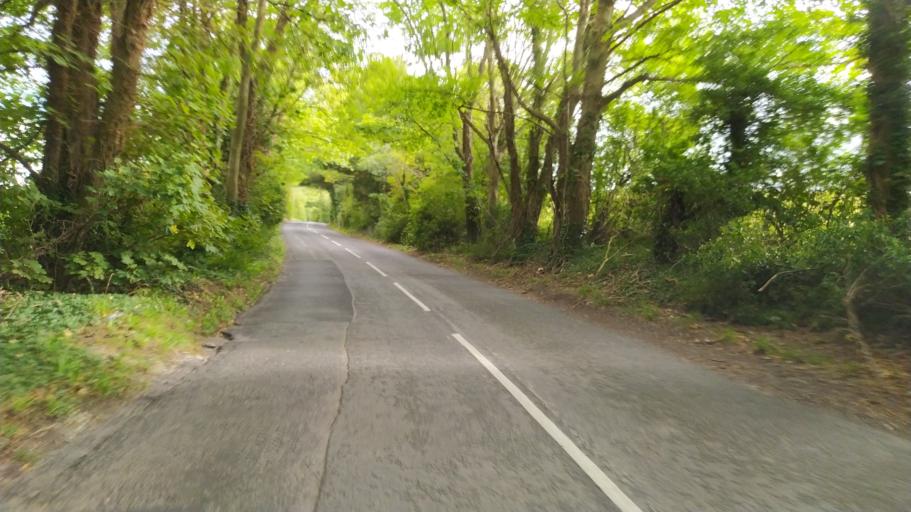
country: GB
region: England
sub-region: Hampshire
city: East Dean
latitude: 51.0877
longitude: -1.5650
